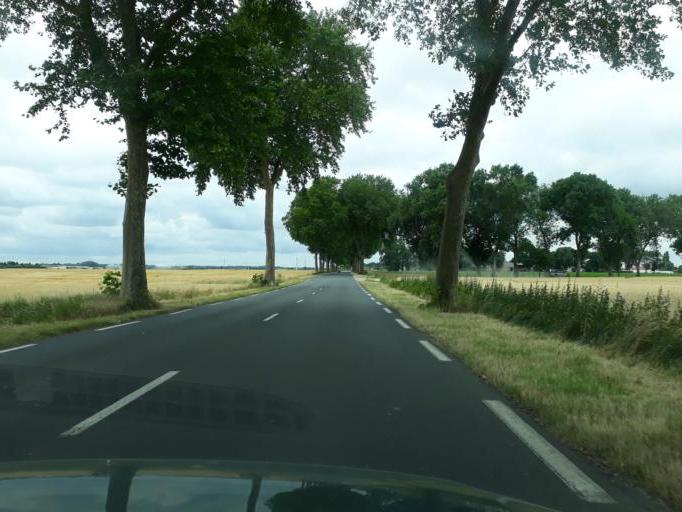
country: FR
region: Centre
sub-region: Departement du Loiret
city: Saint-Denis-en-Val
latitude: 47.8584
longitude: 1.9880
